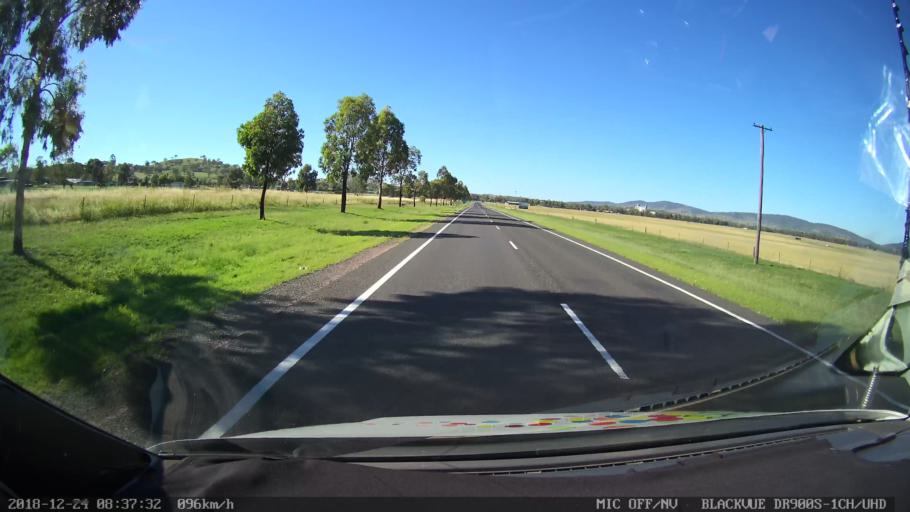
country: AU
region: New South Wales
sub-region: Liverpool Plains
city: Quirindi
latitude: -31.3302
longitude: 150.6486
